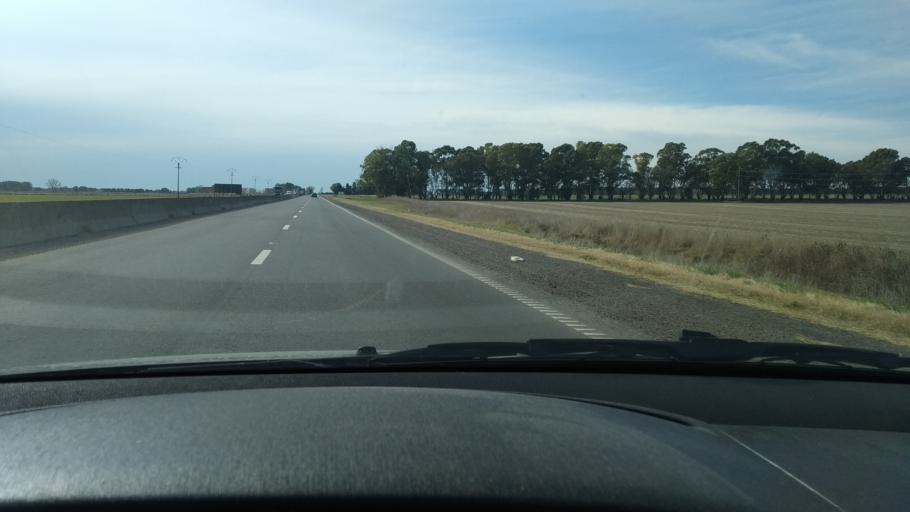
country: AR
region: Buenos Aires
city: Olavarria
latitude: -36.9105
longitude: -60.1970
